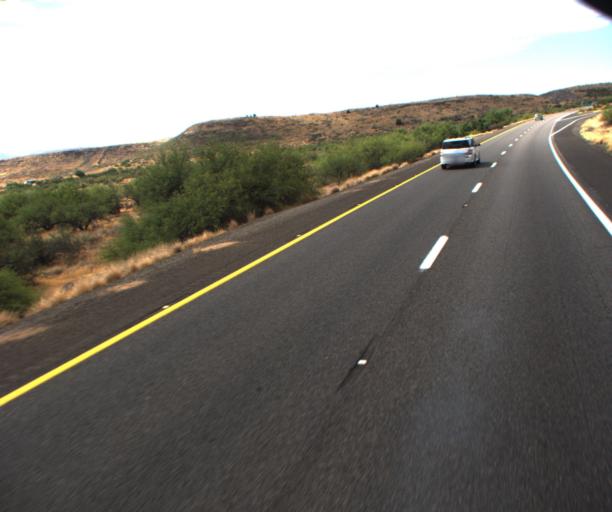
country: US
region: Arizona
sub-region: Yavapai County
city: Cordes Lakes
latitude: 34.2410
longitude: -112.1144
